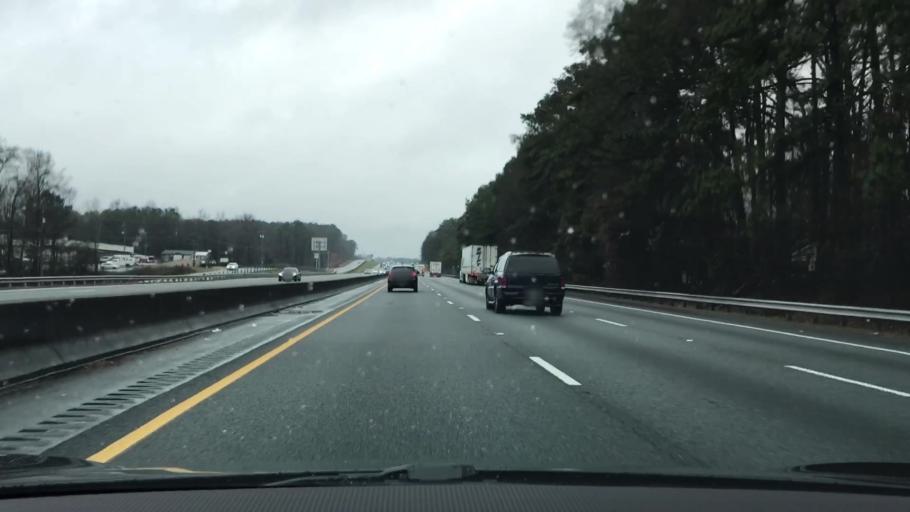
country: US
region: Georgia
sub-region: Newton County
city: Porterdale
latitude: 33.6187
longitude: -83.9283
